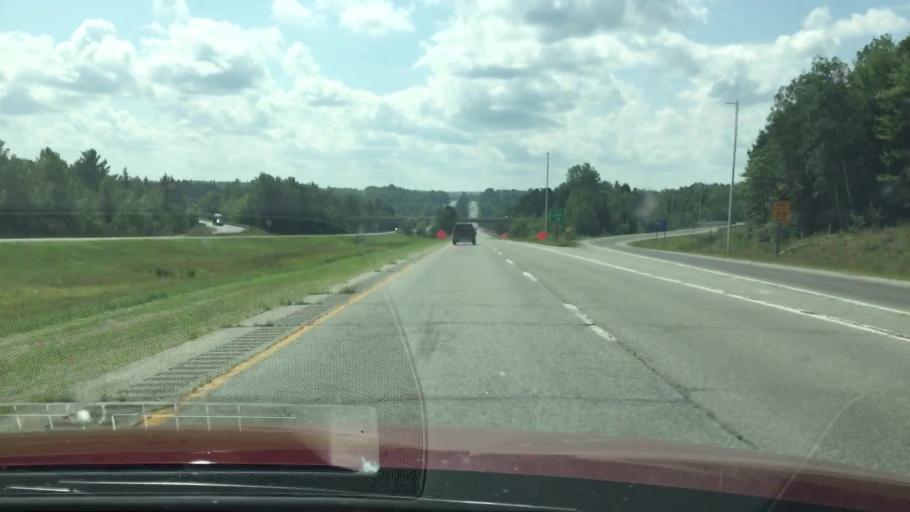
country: US
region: Maine
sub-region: Penobscot County
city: Medway
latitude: 45.6098
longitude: -68.5189
